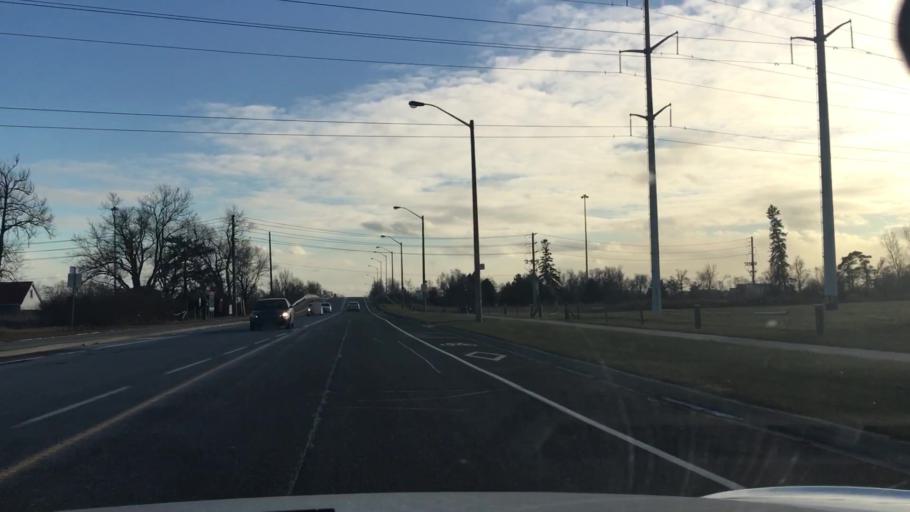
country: CA
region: Ontario
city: Scarborough
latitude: 43.8002
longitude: -79.1884
